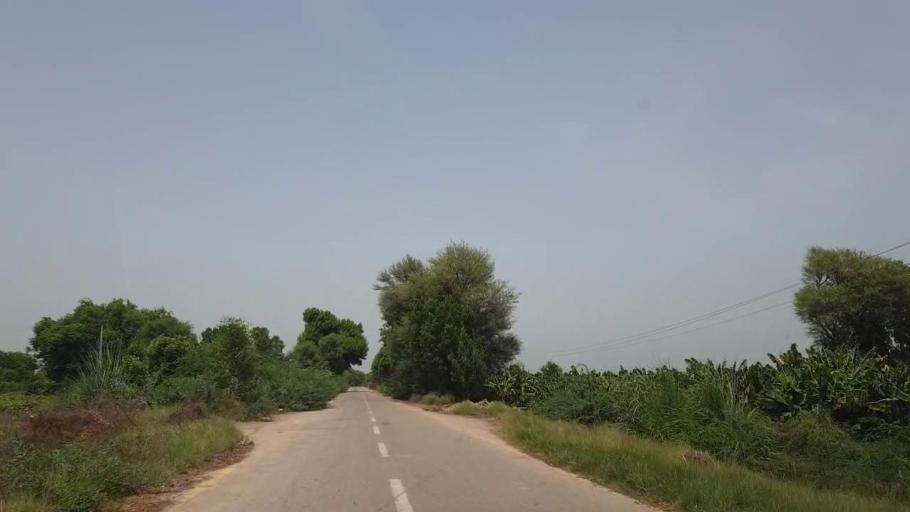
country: PK
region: Sindh
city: Sakrand
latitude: 26.2002
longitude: 68.2418
